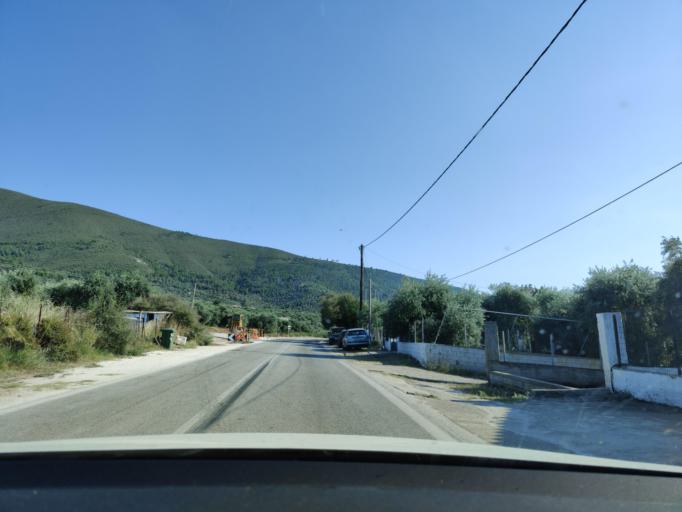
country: GR
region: East Macedonia and Thrace
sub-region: Nomos Kavalas
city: Prinos
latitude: 40.6889
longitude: 24.5267
